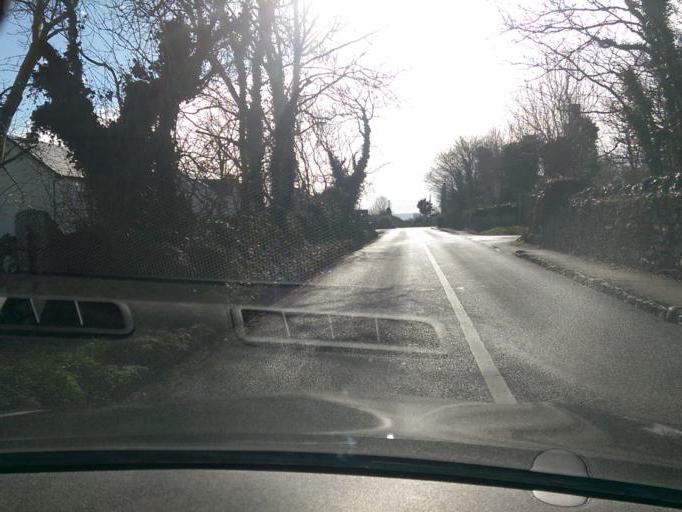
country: IE
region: Connaught
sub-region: County Galway
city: Oranmore
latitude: 53.2460
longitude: -8.9537
